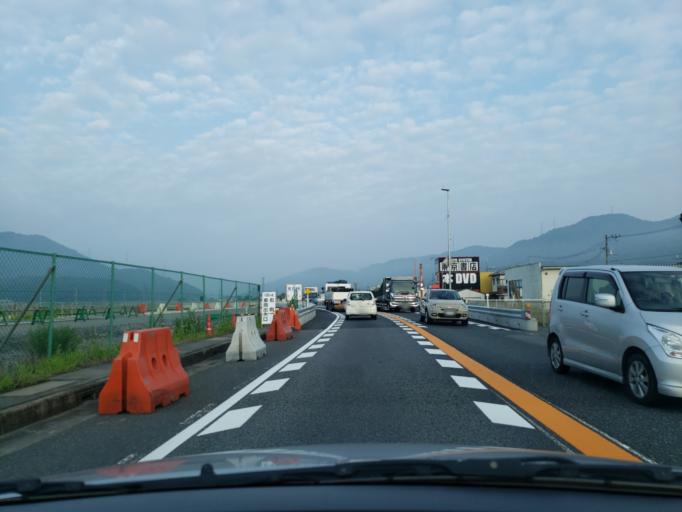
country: JP
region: Hyogo
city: Aioi
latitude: 34.8326
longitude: 134.4313
